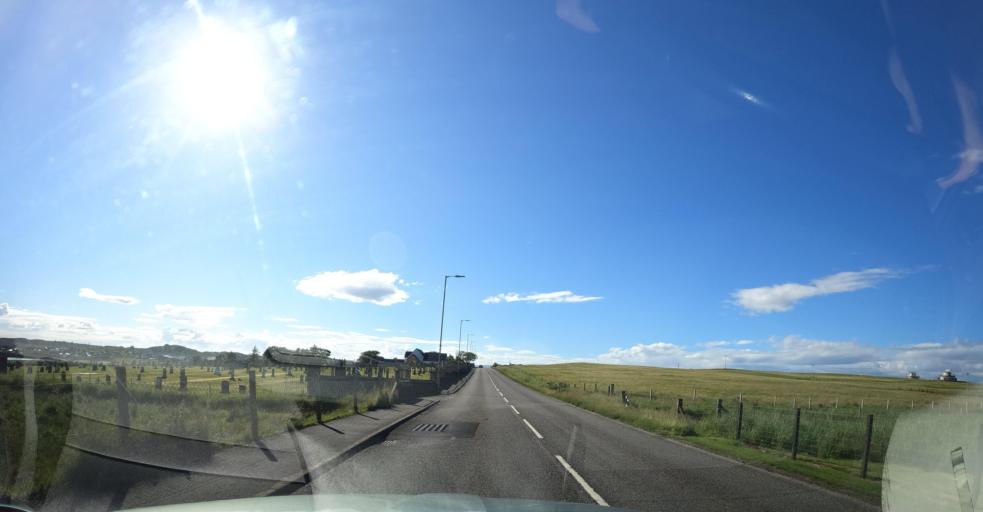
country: GB
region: Scotland
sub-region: Eilean Siar
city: Stornoway
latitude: 58.2067
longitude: -6.3577
